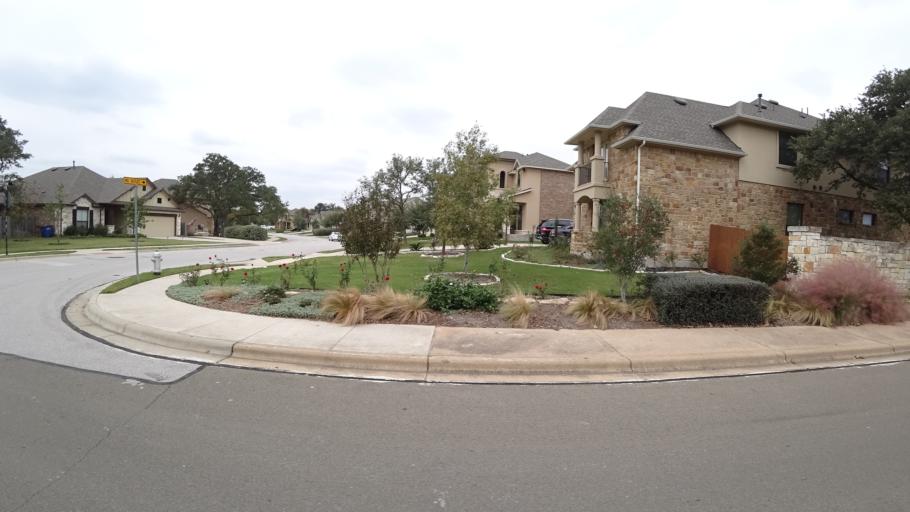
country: US
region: Texas
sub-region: Travis County
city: Shady Hollow
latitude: 30.2096
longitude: -97.8880
